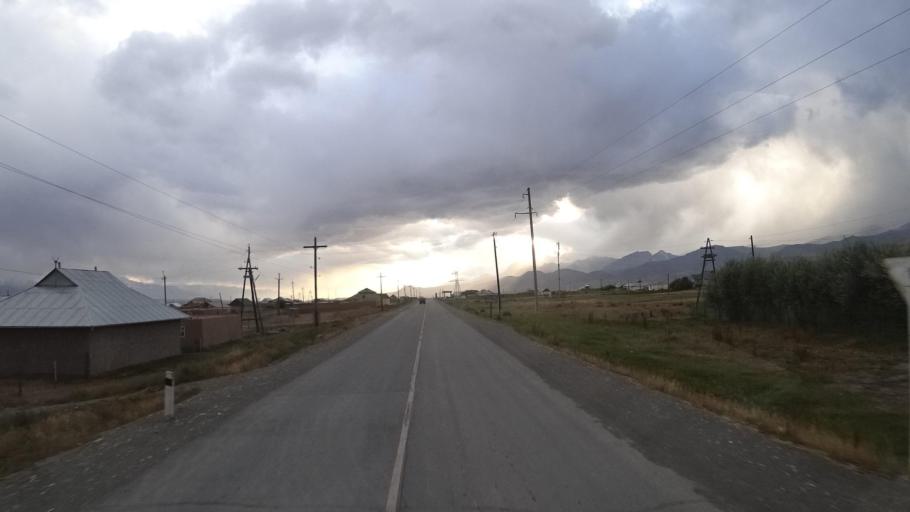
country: KG
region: Osh
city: Osh
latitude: 39.6780
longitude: 72.8883
